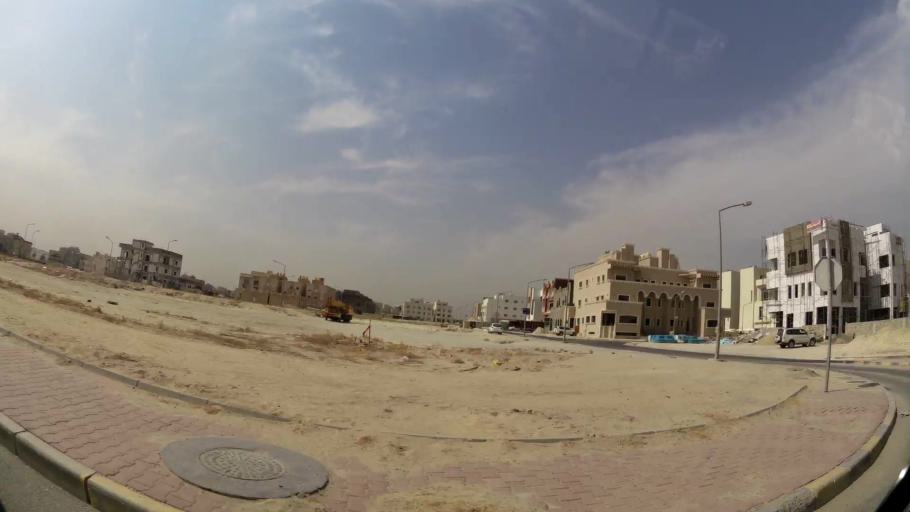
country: KW
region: Al Farwaniyah
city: Janub as Surrah
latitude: 29.2920
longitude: 47.9977
